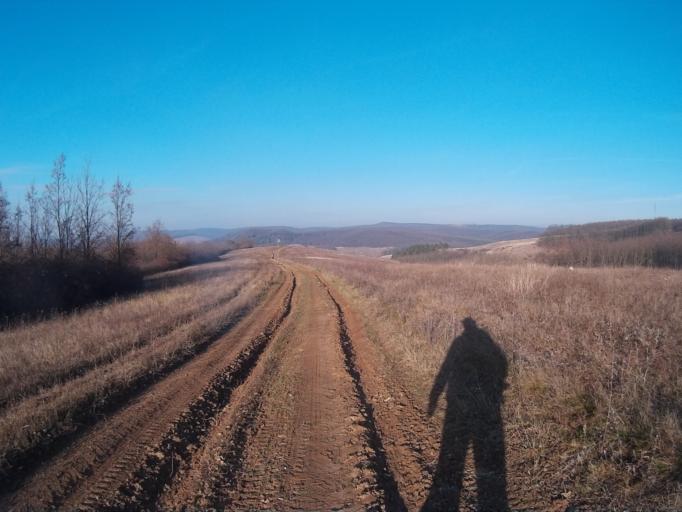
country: HU
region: Nograd
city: Bercel
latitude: 47.9662
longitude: 19.4400
